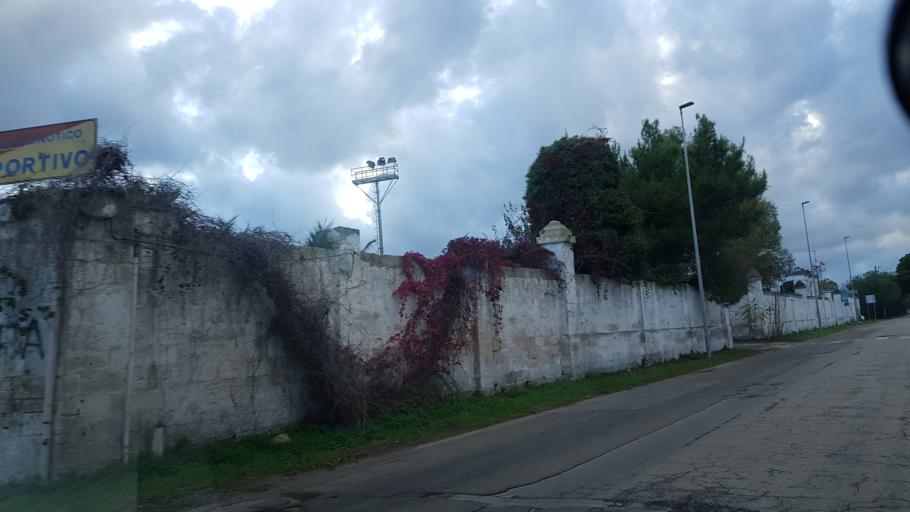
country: IT
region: Apulia
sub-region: Provincia di Brindisi
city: San Pietro Vernotico
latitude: 40.4878
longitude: 18.0060
